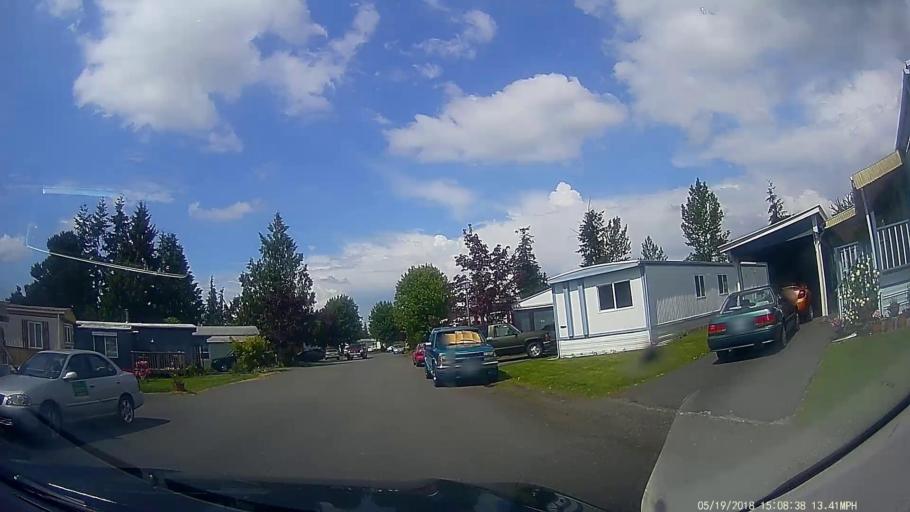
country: US
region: Washington
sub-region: Skagit County
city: Mount Vernon
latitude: 48.4194
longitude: -122.3070
